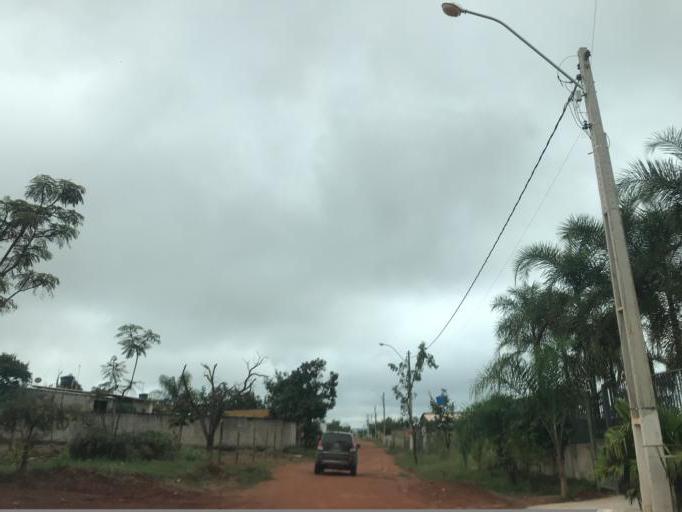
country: BR
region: Federal District
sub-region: Brasilia
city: Brasilia
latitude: -15.8267
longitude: -47.7898
